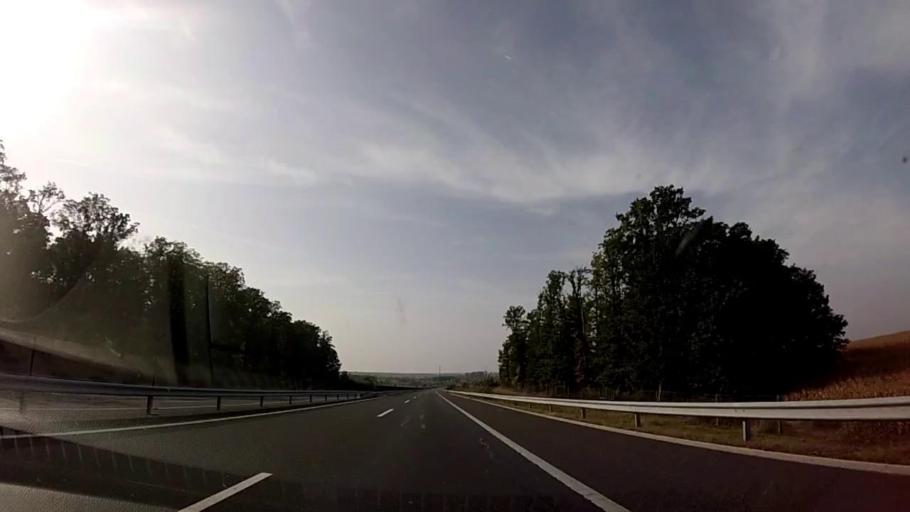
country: HU
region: Somogy
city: Balatonbereny
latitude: 46.6566
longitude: 17.3099
